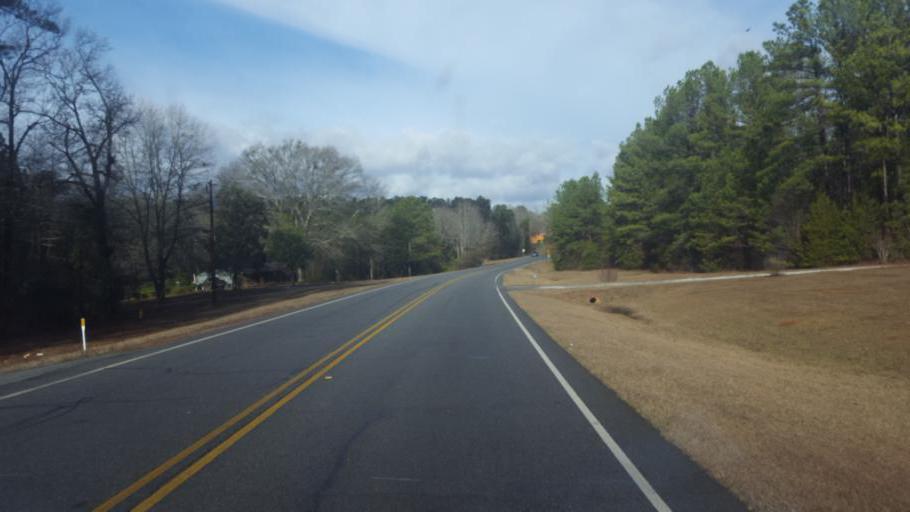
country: US
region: Georgia
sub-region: Butts County
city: Indian Springs
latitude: 33.2518
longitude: -83.8962
